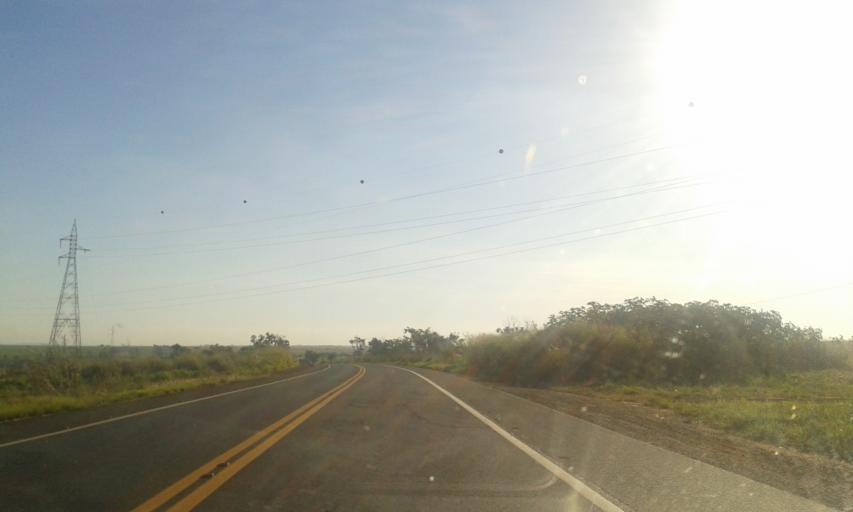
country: BR
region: Minas Gerais
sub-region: Ituiutaba
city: Ituiutaba
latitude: -18.8807
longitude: -49.1944
